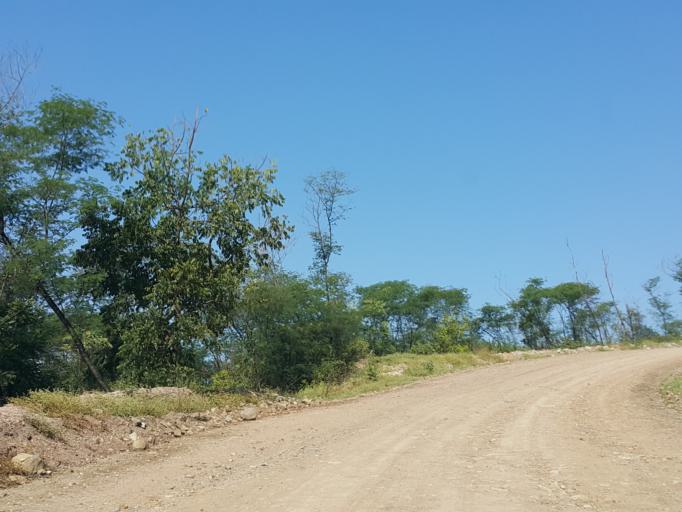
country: TH
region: Lampang
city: Mae Mo
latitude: 18.3260
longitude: 99.7373
